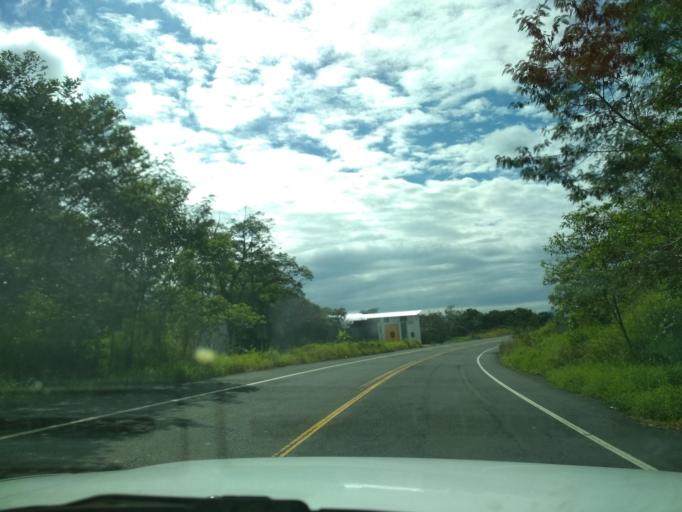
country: MX
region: Veracruz
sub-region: Coatepec
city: Las Lomas
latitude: 19.4509
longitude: -96.9276
